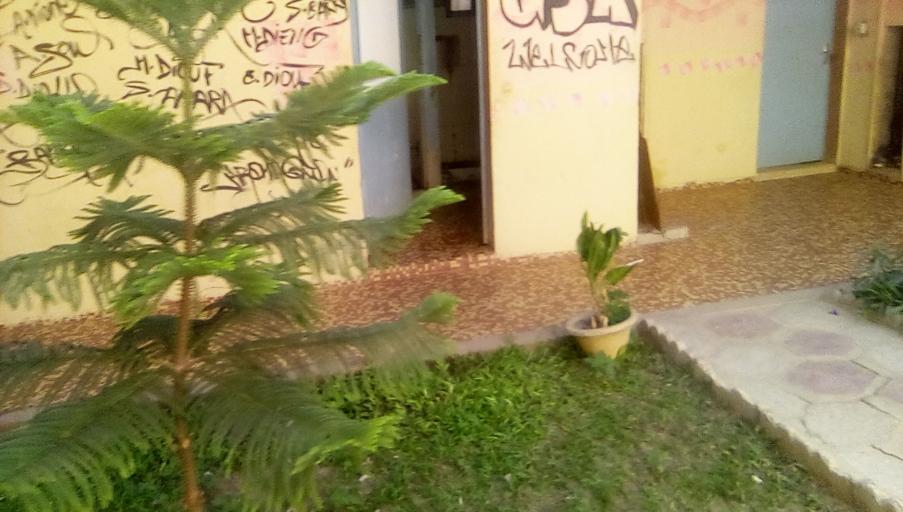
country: SN
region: Saint-Louis
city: Saint-Louis
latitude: 16.0643
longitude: -16.4190
